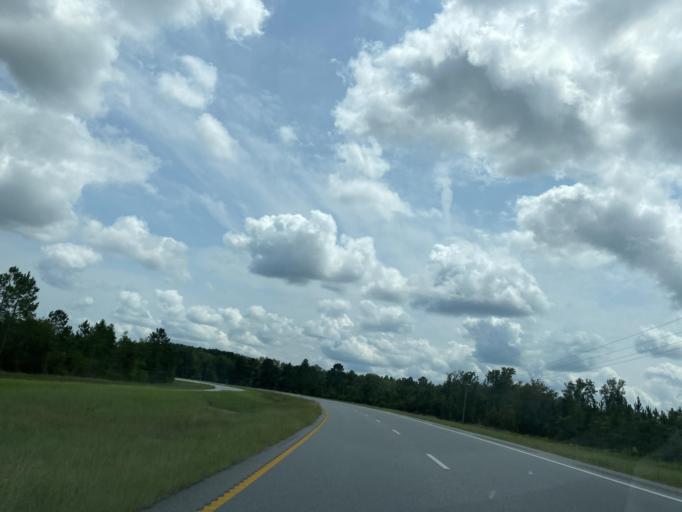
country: US
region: Georgia
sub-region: Ware County
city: Deenwood
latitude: 31.2794
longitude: -82.4512
